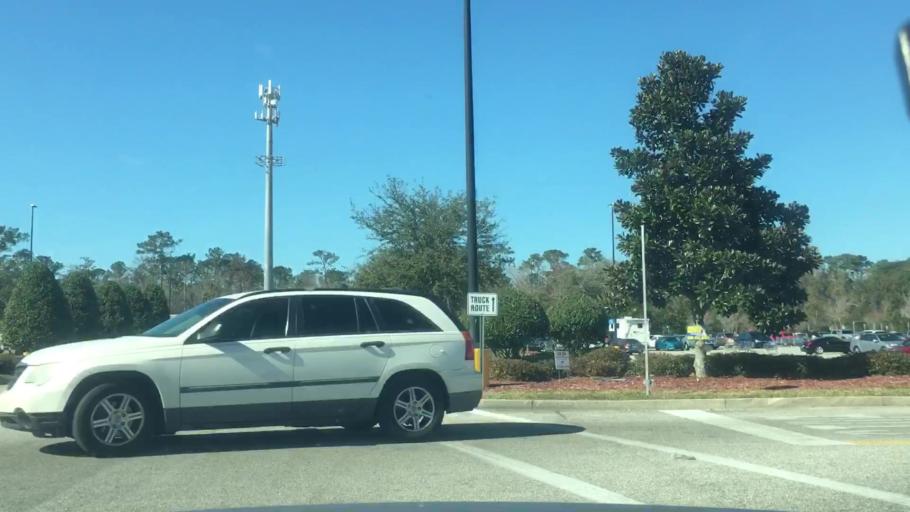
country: US
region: Florida
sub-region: Saint Johns County
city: Fruit Cove
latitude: 30.1778
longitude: -81.5567
